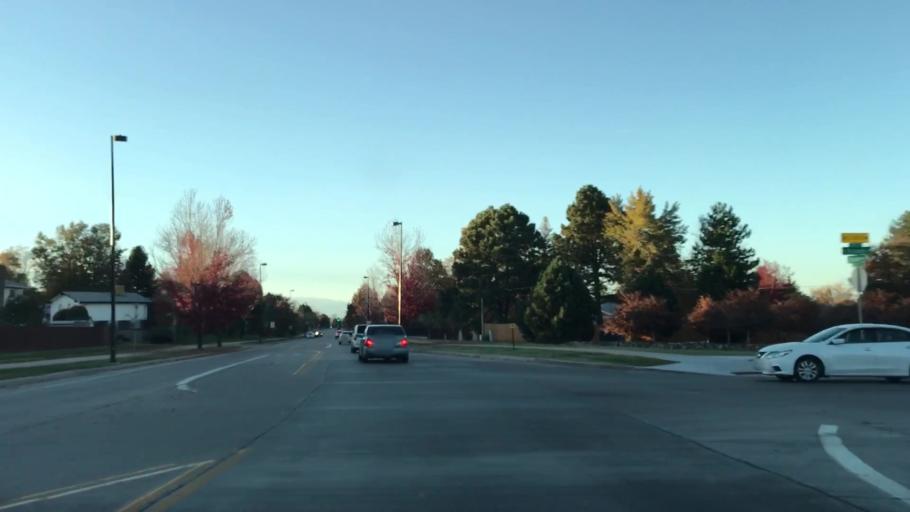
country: US
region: Colorado
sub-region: Arapahoe County
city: Glendale
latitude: 39.6602
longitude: -104.8849
